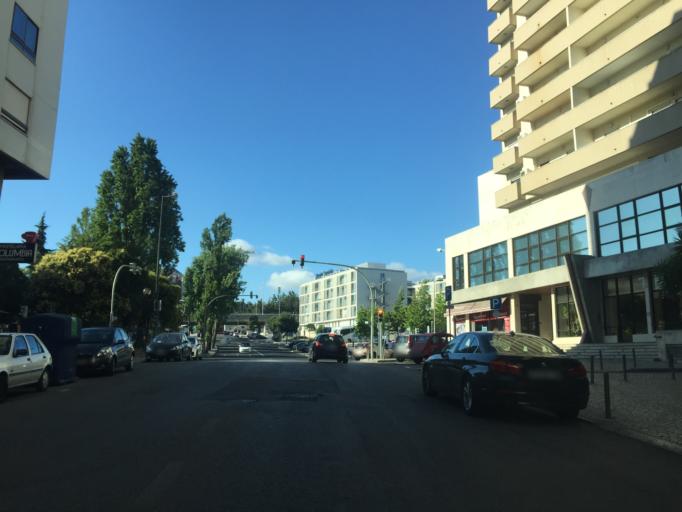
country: PT
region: Lisbon
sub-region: Odivelas
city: Pontinha
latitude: 38.7478
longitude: -9.1806
